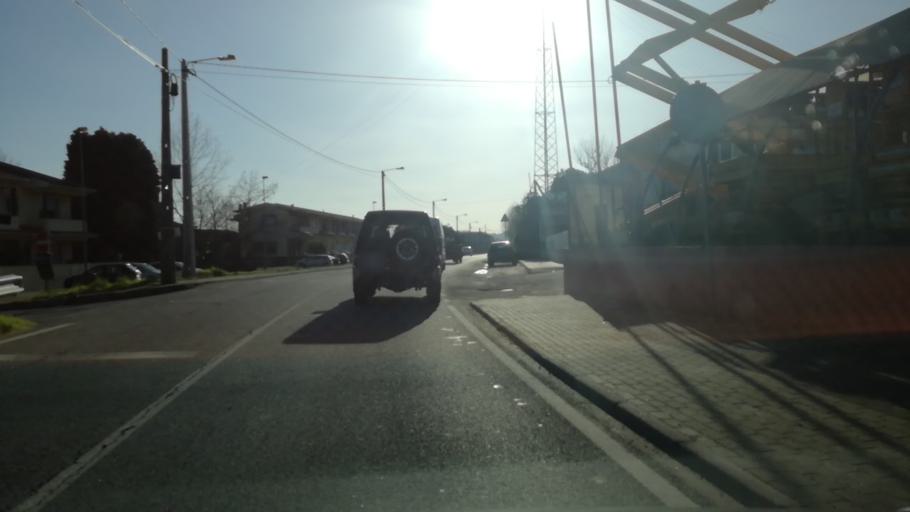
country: PT
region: Braga
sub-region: Guimaraes
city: Ponte
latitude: 41.4967
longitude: -8.3350
